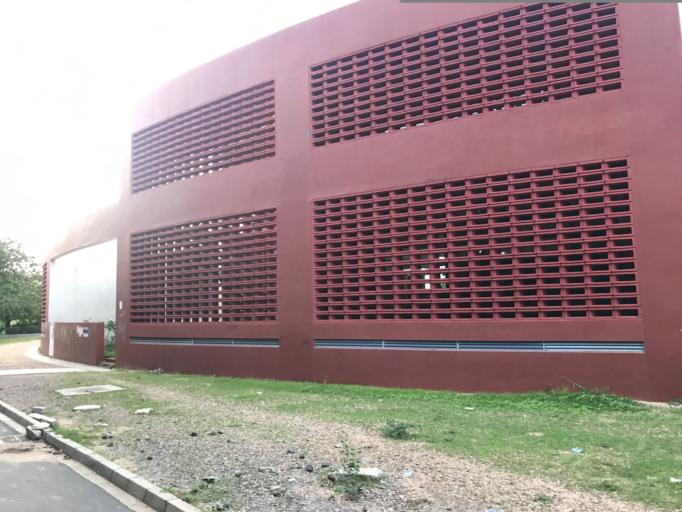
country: SN
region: Dakar
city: Dakar
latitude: 14.6850
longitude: -17.4618
